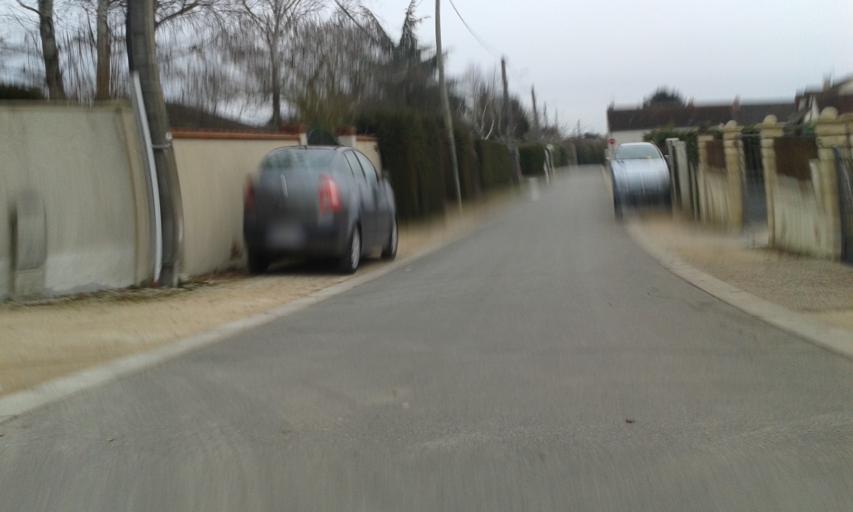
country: FR
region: Centre
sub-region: Departement du Loiret
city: Beaugency
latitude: 47.7991
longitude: 1.6006
